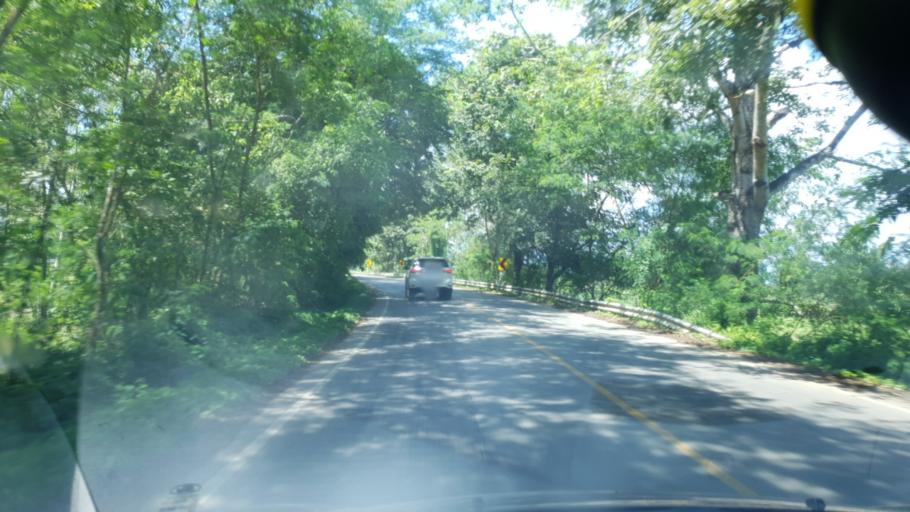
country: TH
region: Chiang Rai
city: Wiang Chai
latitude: 19.9593
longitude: 99.9488
